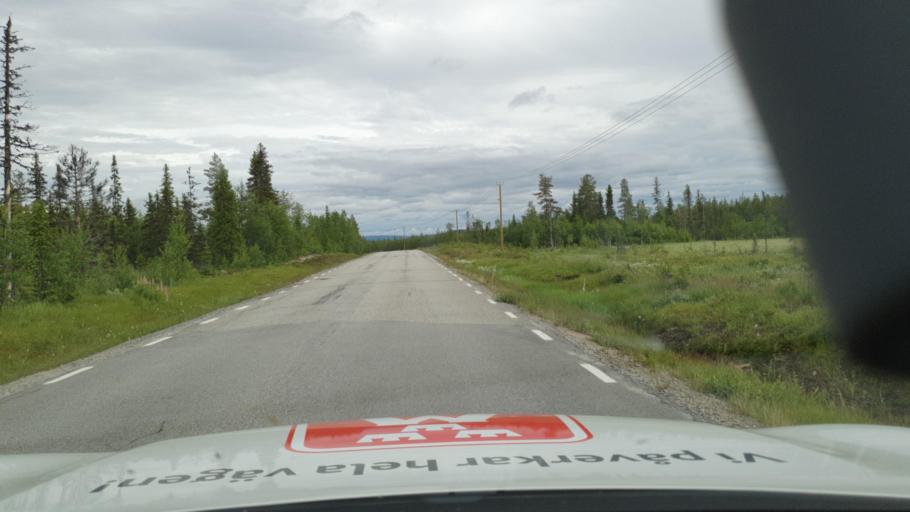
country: SE
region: Vaesterbotten
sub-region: Lycksele Kommun
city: Soderfors
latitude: 64.3829
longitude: 18.0191
